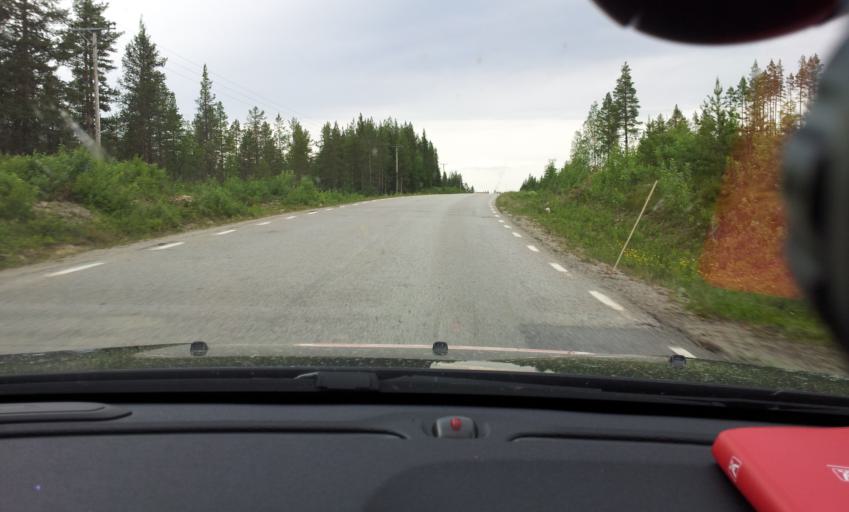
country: SE
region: Jaemtland
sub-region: Bergs Kommun
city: Hoverberg
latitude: 62.6949
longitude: 14.6275
